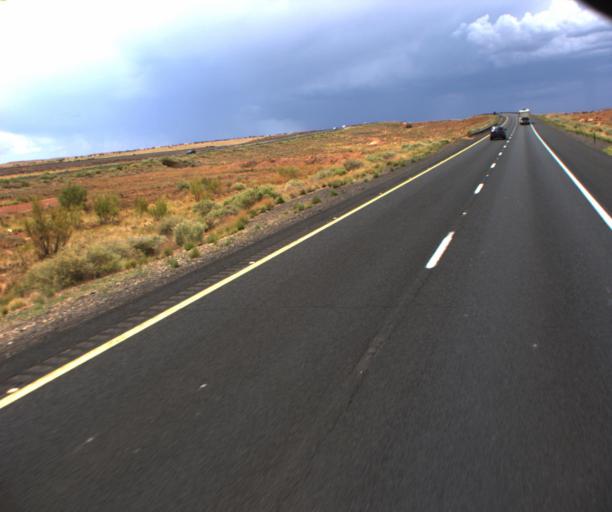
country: US
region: Arizona
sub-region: Coconino County
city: LeChee
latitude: 35.0995
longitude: -110.9652
